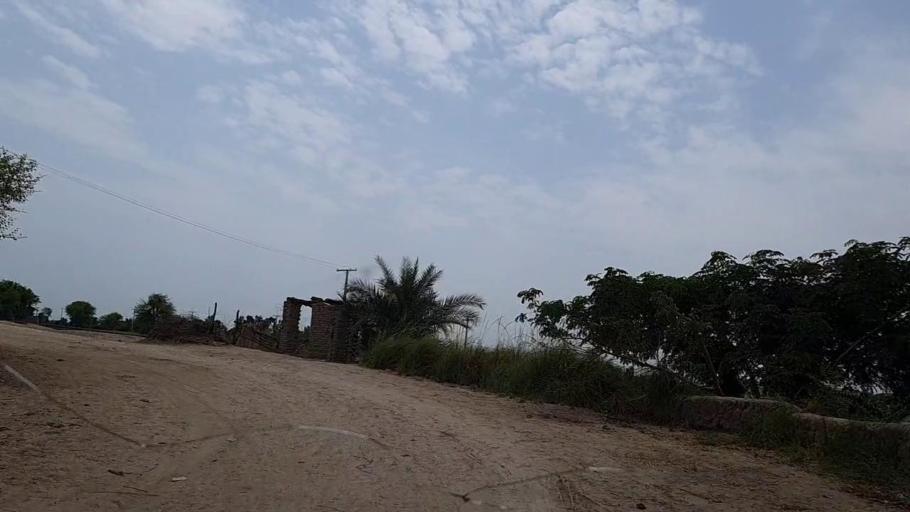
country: PK
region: Sindh
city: Tharu Shah
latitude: 26.9239
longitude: 68.0820
